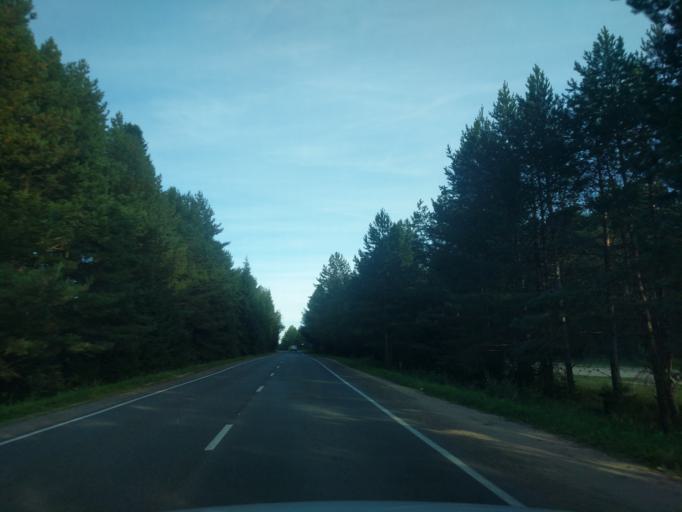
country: RU
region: Kirov
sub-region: Kirovo-Chepetskiy Rayon
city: Kirov
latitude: 58.6054
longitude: 49.8124
